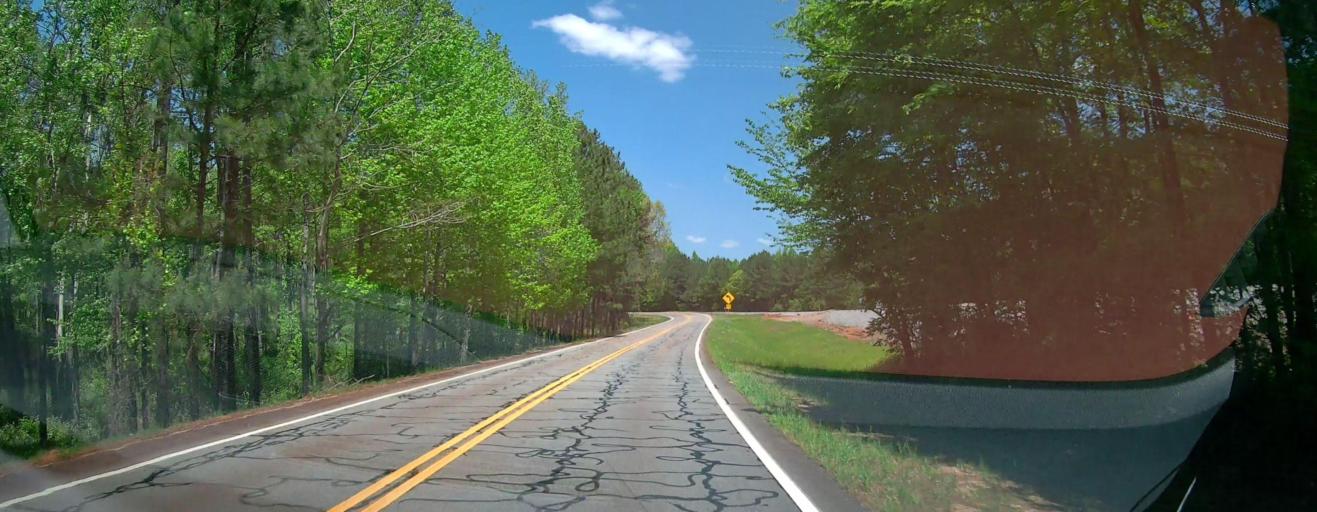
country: US
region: Georgia
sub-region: Jones County
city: Gray
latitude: 33.1335
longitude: -83.6313
